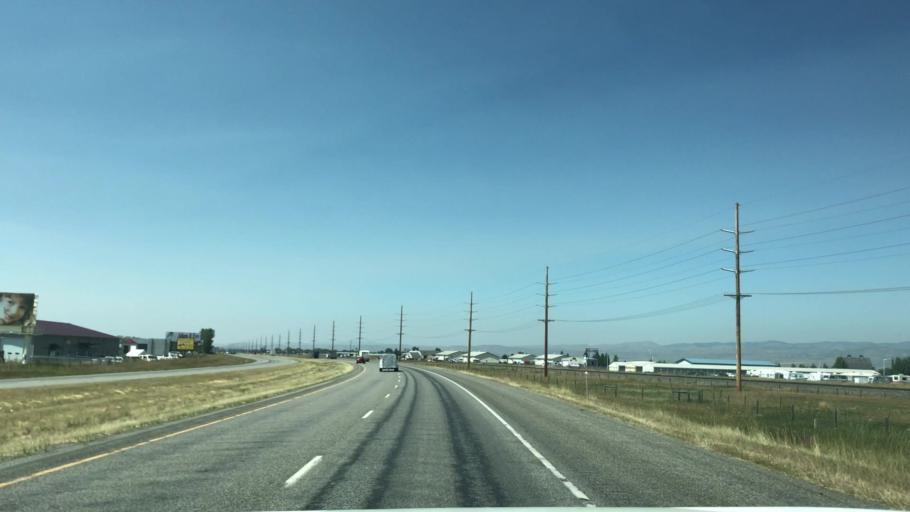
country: US
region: Montana
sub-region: Gallatin County
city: Belgrade
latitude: 45.7884
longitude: -111.2043
